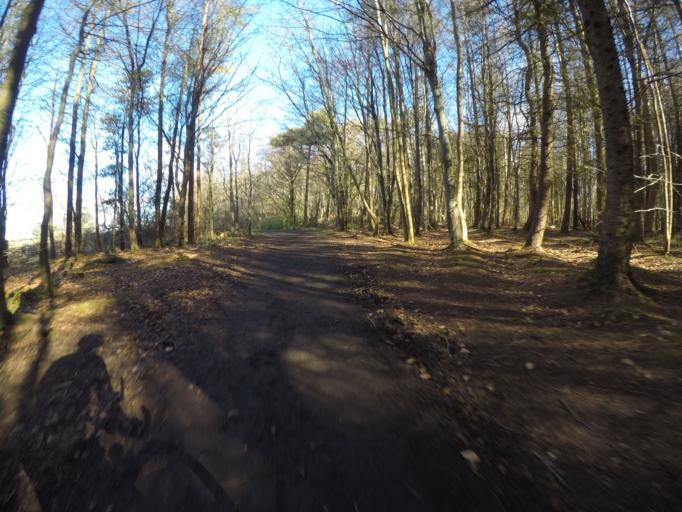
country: GB
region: Scotland
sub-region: North Ayrshire
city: Irvine
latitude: 55.6397
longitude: -4.6567
